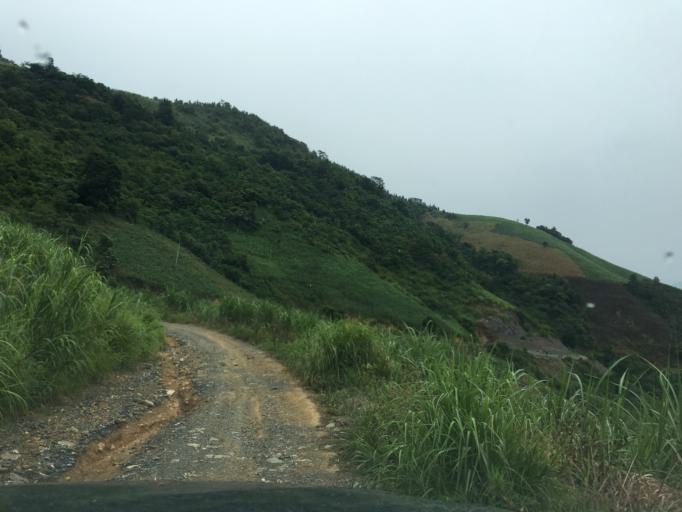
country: CN
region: Guangxi Zhuangzu Zizhiqu
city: Tongle
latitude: 25.0040
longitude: 105.9869
